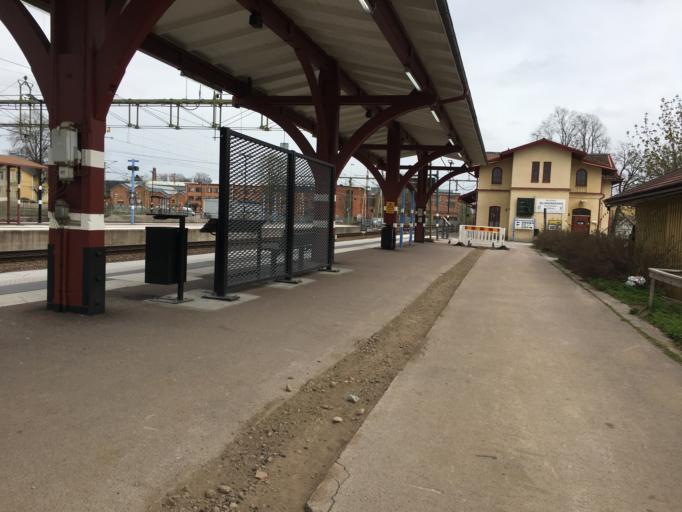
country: SE
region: Vaermland
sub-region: Kristinehamns Kommun
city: Kristinehamn
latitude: 59.3170
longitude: 14.1076
